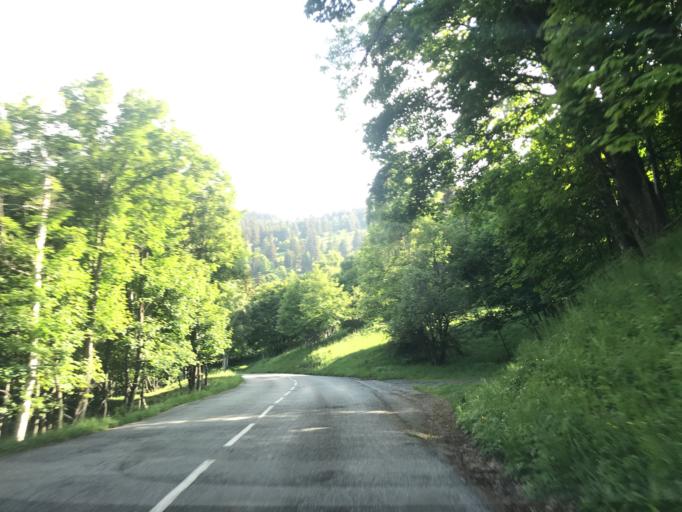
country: FR
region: Rhone-Alpes
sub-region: Departement de la Savoie
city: Modane
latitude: 45.2072
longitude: 6.6376
